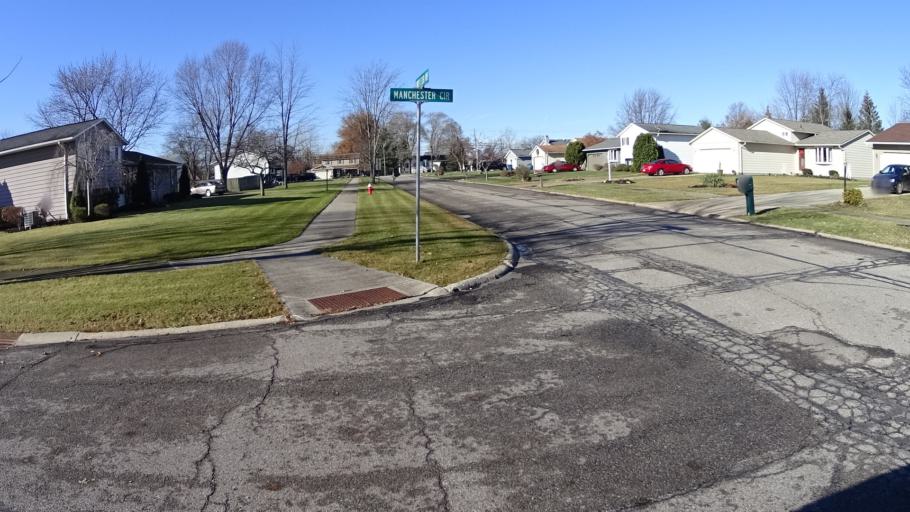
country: US
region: Ohio
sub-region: Lorain County
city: North Ridgeville
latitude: 41.4166
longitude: -82.0172
